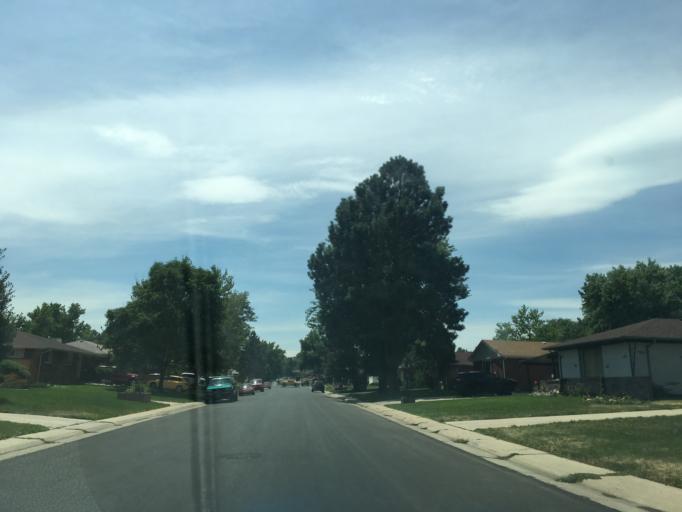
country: US
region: Colorado
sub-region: Jefferson County
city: Lakewood
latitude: 39.6807
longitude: -105.0511
